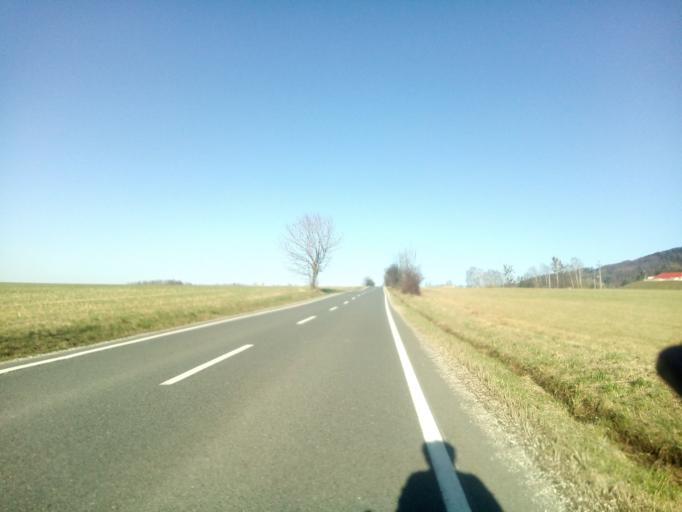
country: CZ
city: Raskovice
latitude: 49.6419
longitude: 18.4593
